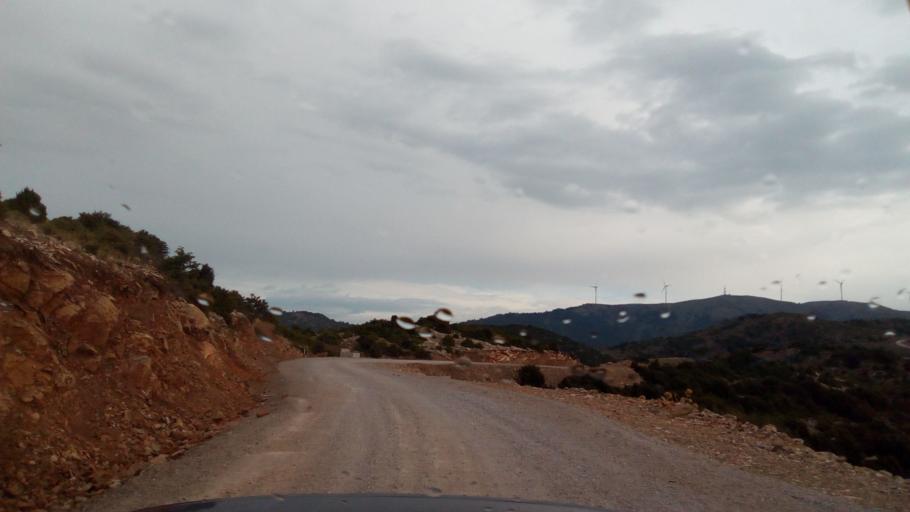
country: GR
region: West Greece
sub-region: Nomos Achaias
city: Kamarai
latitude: 38.4299
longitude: 22.0500
